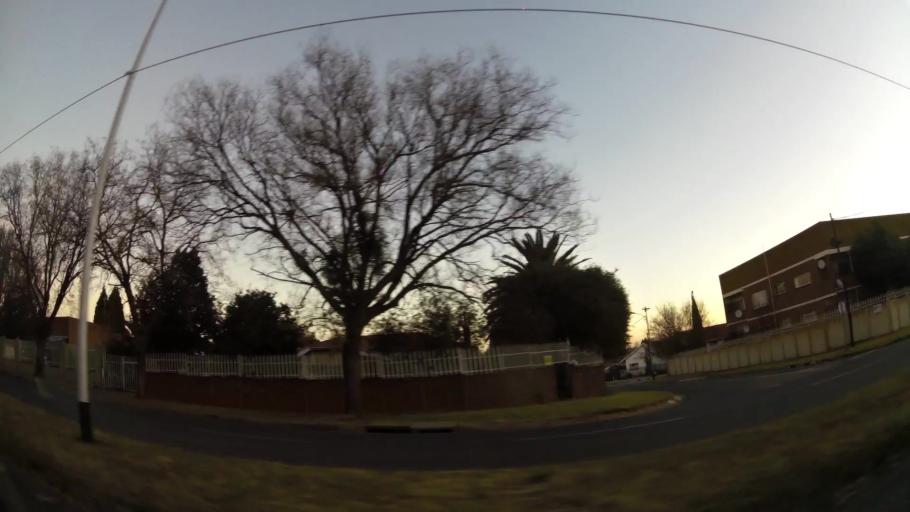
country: ZA
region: Gauteng
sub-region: City of Johannesburg Metropolitan Municipality
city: Roodepoort
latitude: -26.1675
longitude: 27.9077
